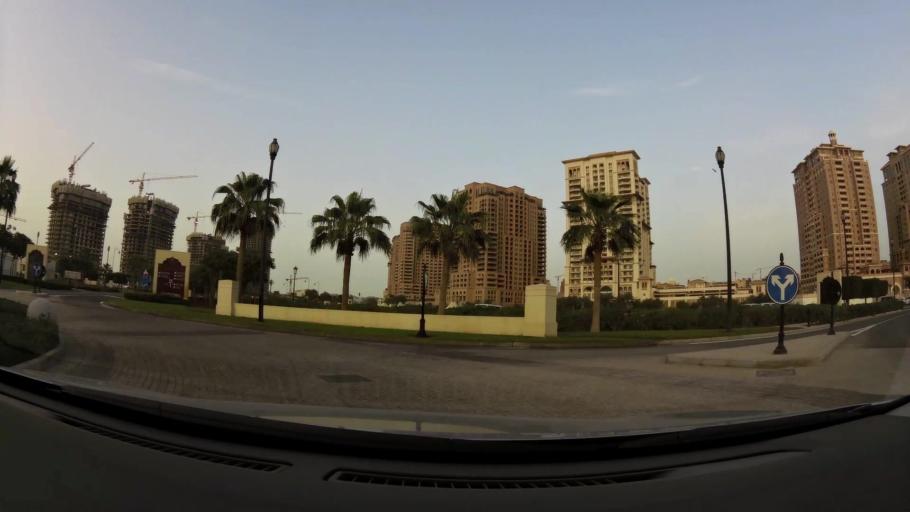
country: QA
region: Baladiyat ad Dawhah
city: Doha
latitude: 25.3700
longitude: 51.5360
